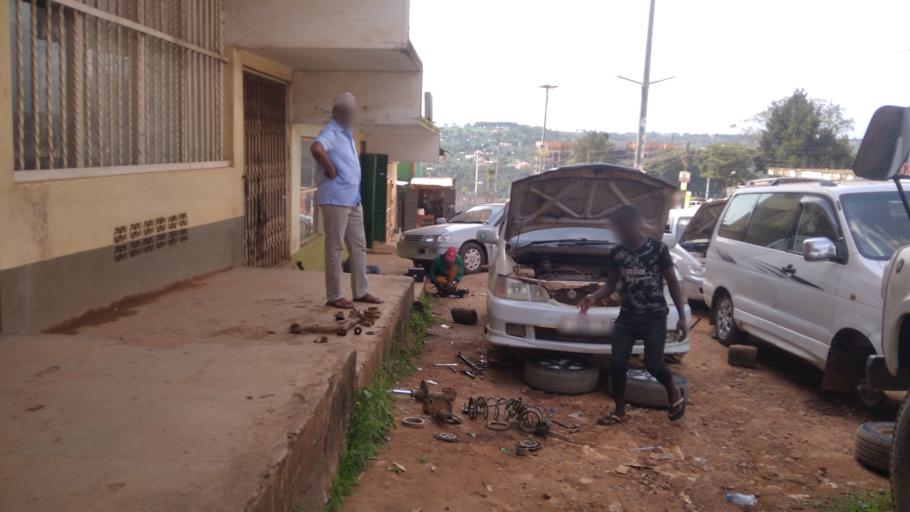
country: UG
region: Central Region
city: Masaka
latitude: -0.3394
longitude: 31.7386
